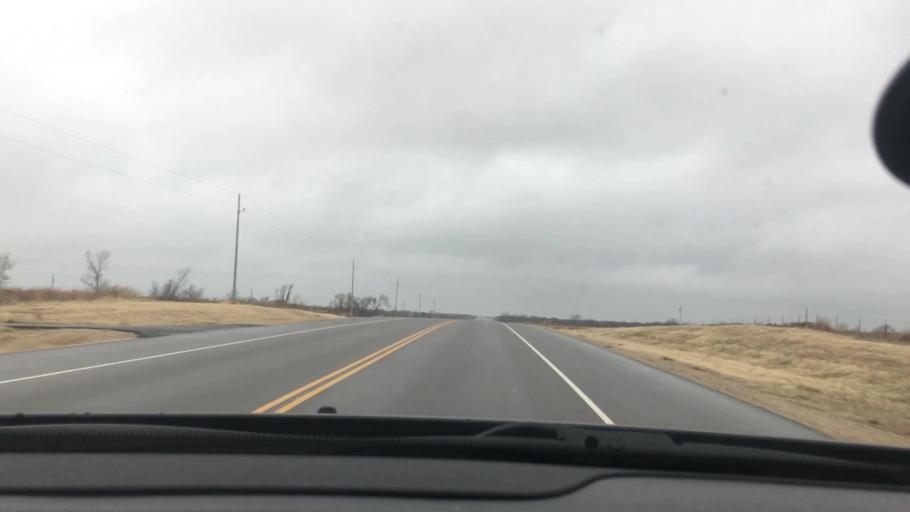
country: US
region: Oklahoma
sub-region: Johnston County
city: Tishomingo
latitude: 34.3426
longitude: -96.6415
